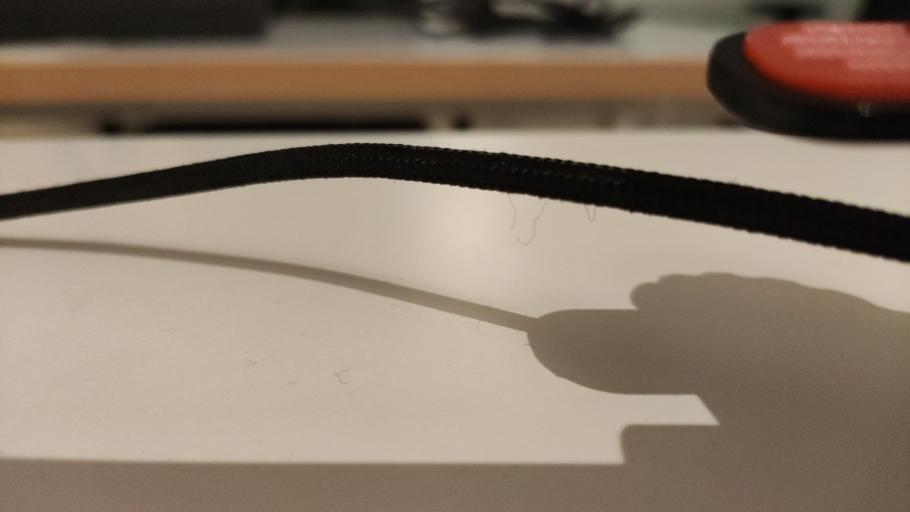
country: RU
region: Moskovskaya
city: Novoye
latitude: 55.6323
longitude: 38.9398
